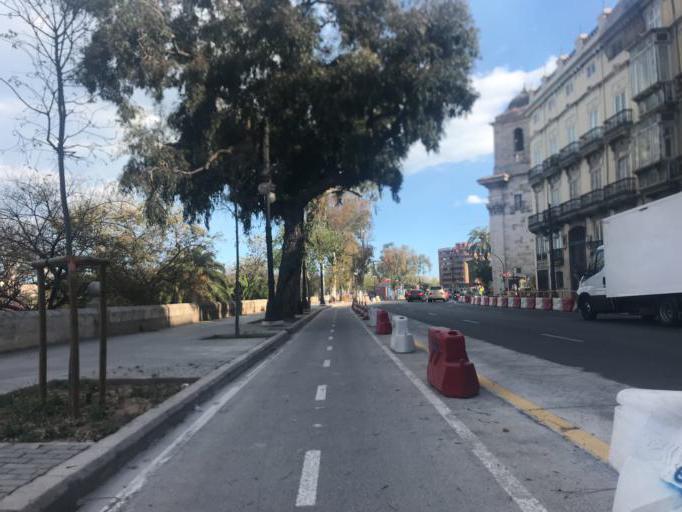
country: ES
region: Valencia
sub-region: Provincia de Valencia
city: Valencia
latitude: 39.4775
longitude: -0.3720
